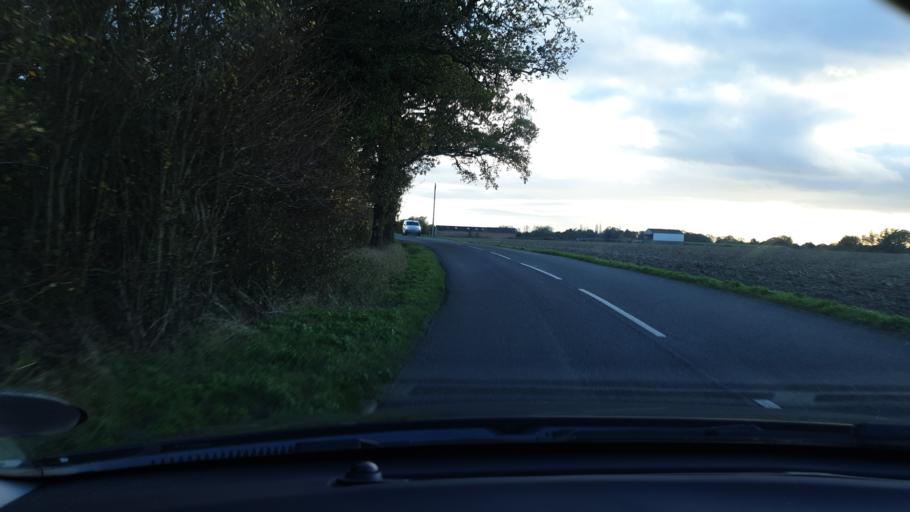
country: GB
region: England
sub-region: Essex
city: Mistley
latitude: 51.9068
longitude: 1.1436
